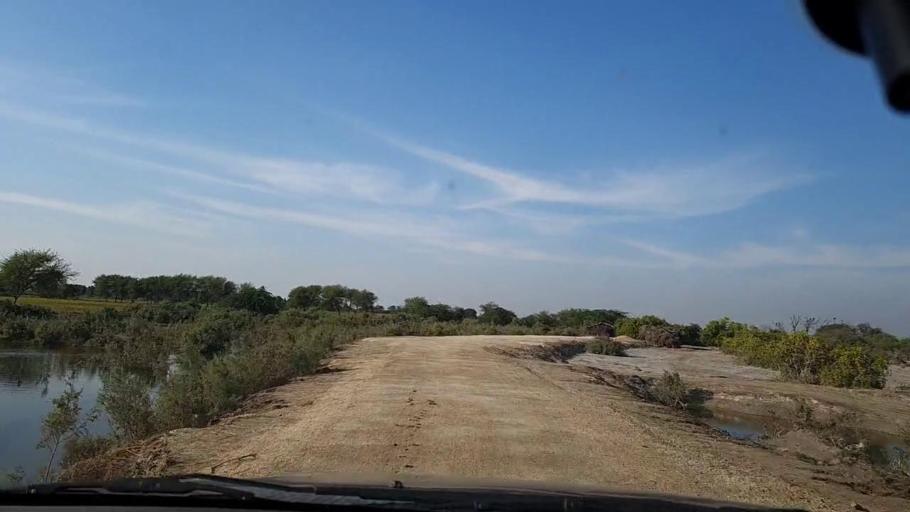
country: PK
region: Sindh
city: Mirpur Batoro
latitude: 24.6363
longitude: 68.2981
